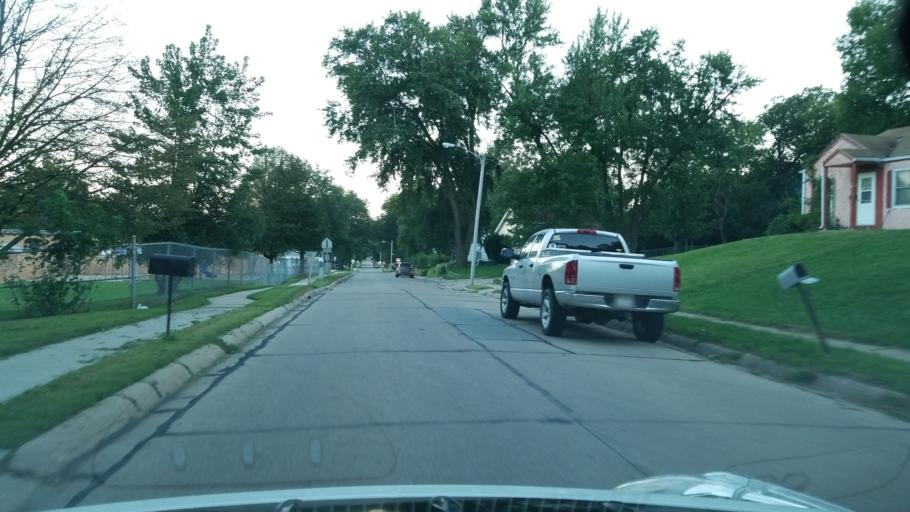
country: US
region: Nebraska
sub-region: Sarpy County
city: Bellevue
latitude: 41.1390
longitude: -95.9003
